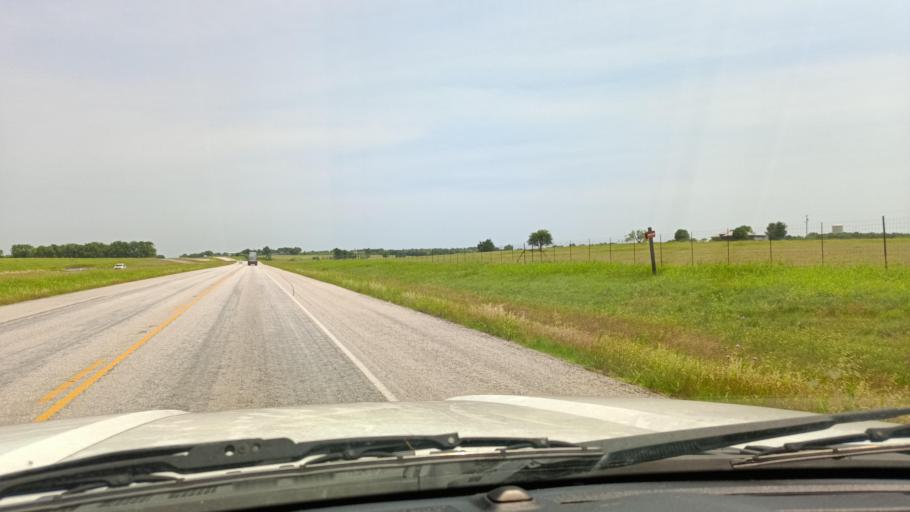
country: US
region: Texas
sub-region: Bell County
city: Rogers
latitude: 30.9594
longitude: -97.2598
